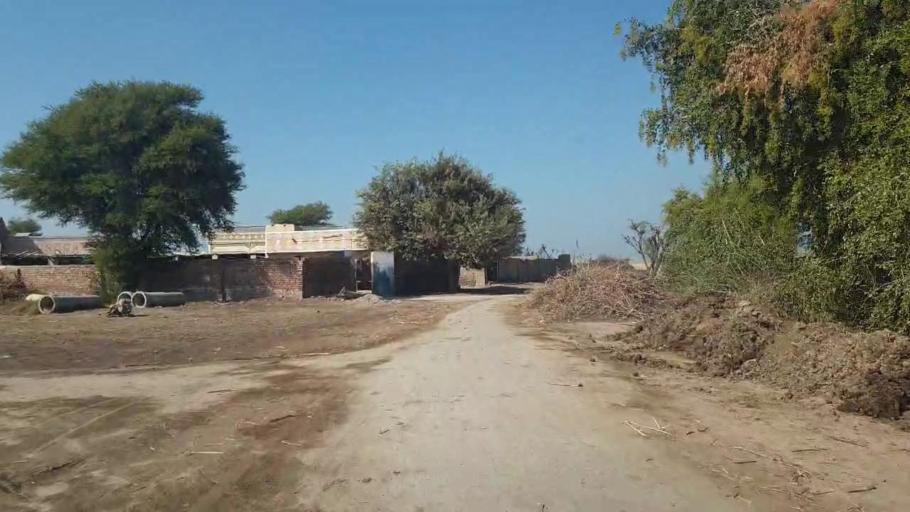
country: PK
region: Sindh
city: Shahdadpur
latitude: 25.9245
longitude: 68.5629
